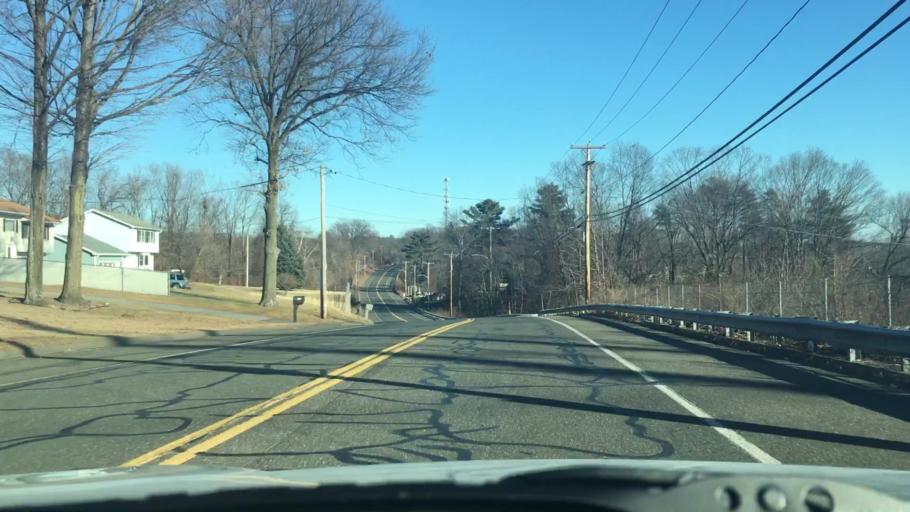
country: US
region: Massachusetts
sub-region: Hampden County
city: Ludlow
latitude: 42.1599
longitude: -72.5376
